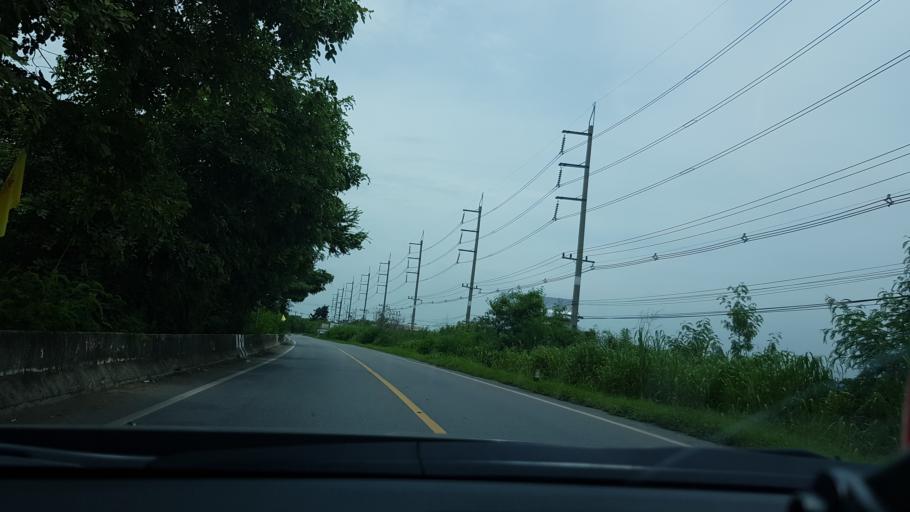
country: TH
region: Pathum Thani
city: Sam Khok
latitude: 14.1422
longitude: 100.5282
